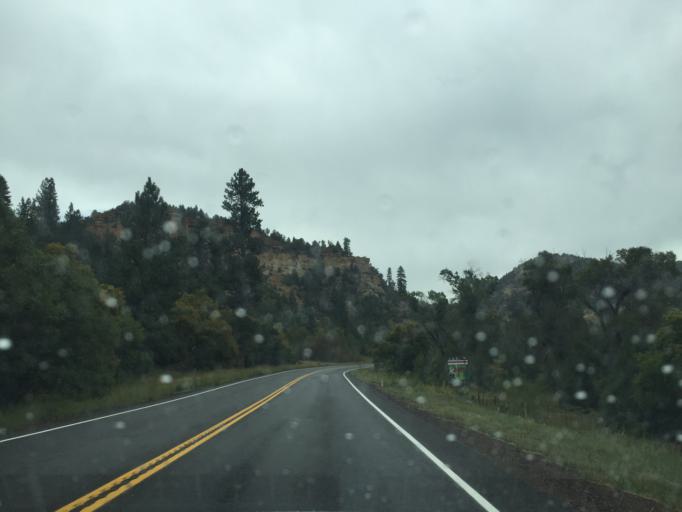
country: US
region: Utah
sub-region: Kane County
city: Kanab
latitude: 37.3715
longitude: -112.5949
